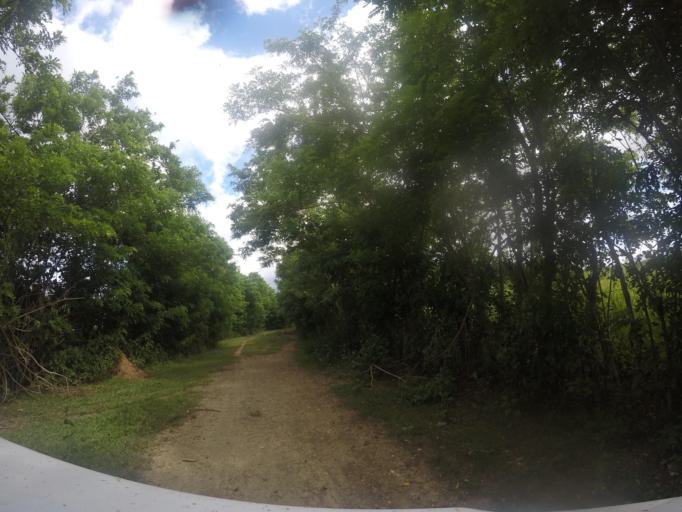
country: TL
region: Lautem
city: Lospalos
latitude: -8.5059
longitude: 127.0093
